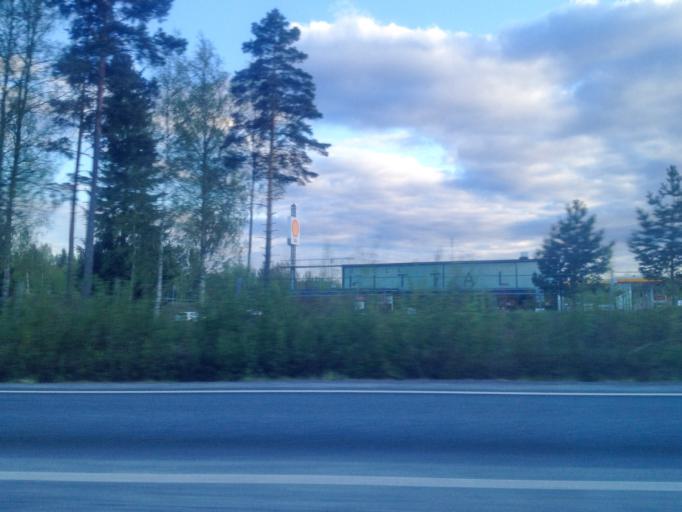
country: FI
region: Haeme
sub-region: Haemeenlinna
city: Kalvola
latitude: 61.0985
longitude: 24.1644
